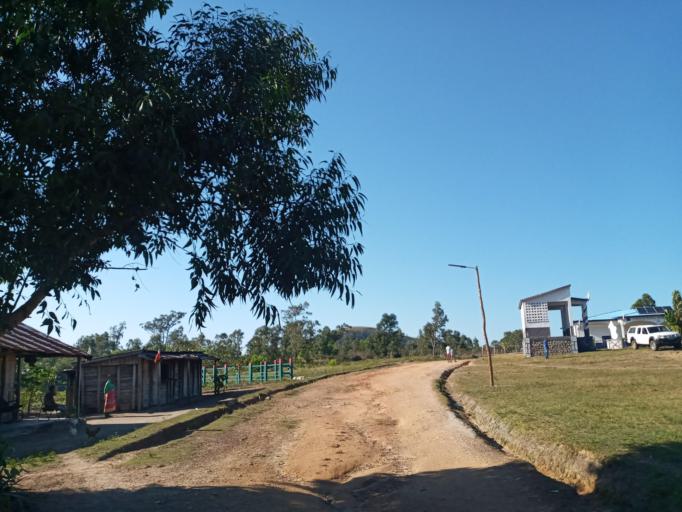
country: MG
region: Anosy
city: Fort Dauphin
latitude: -24.9103
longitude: 47.0332
